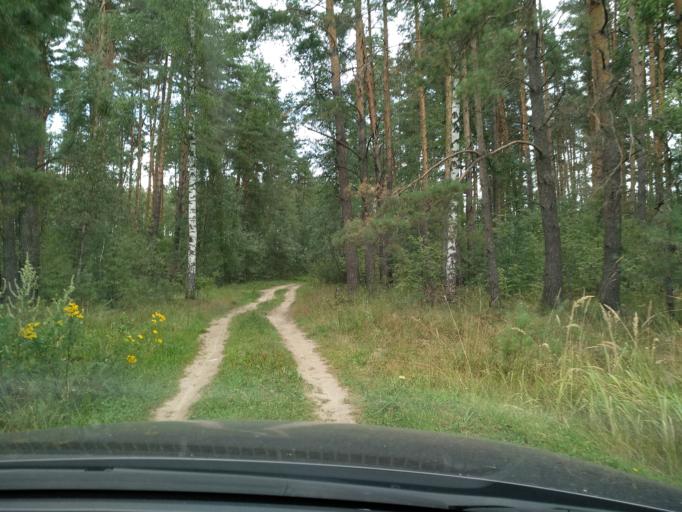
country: RU
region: Moskovskaya
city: Krasnyy Tkach
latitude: 55.3801
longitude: 39.2356
